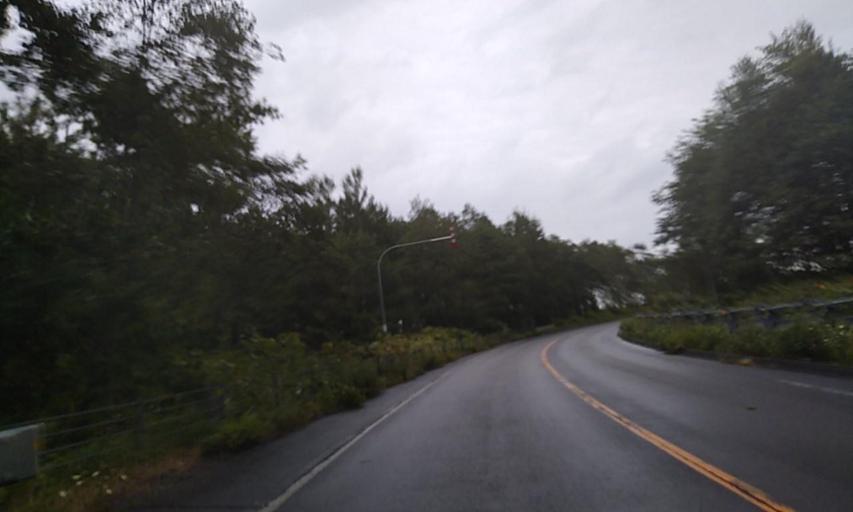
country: JP
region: Hokkaido
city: Mombetsu
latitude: 44.4886
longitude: 143.0920
